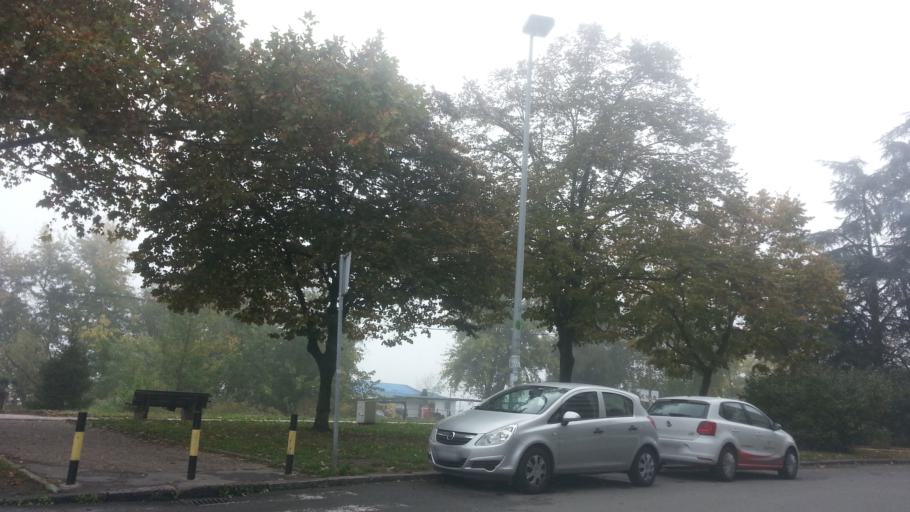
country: RS
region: Central Serbia
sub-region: Belgrade
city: Zemun
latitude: 44.8388
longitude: 20.4184
